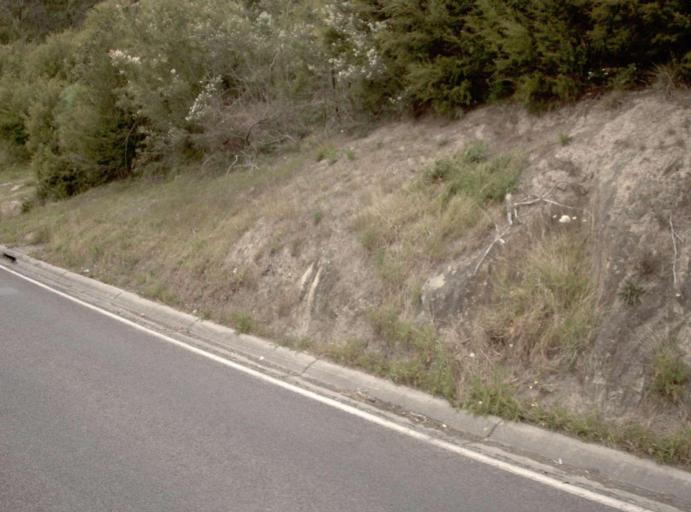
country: AU
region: Victoria
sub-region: Yarra Ranges
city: Millgrove
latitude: -37.7591
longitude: 145.6489
